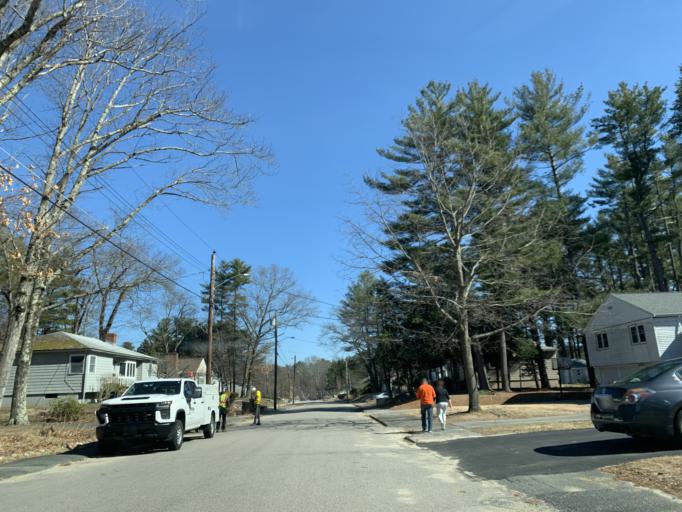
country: US
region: Massachusetts
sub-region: Norfolk County
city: Sharon
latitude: 42.1155
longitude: -71.1882
